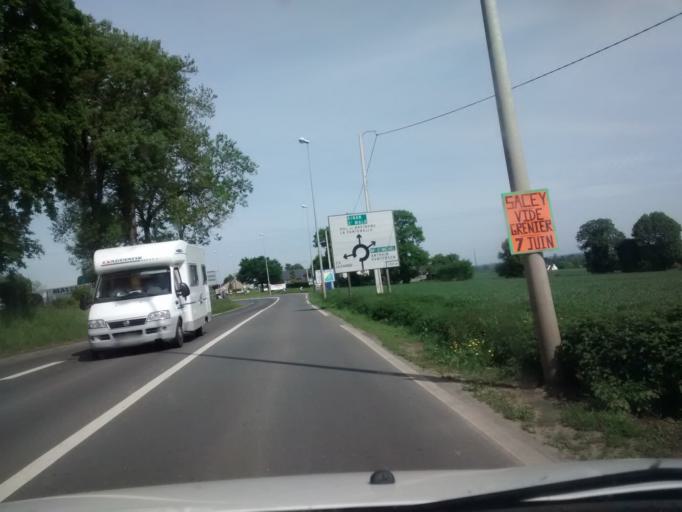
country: FR
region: Brittany
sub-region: Departement d'Ille-et-Vilaine
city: Antrain
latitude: 48.4487
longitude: -1.4749
